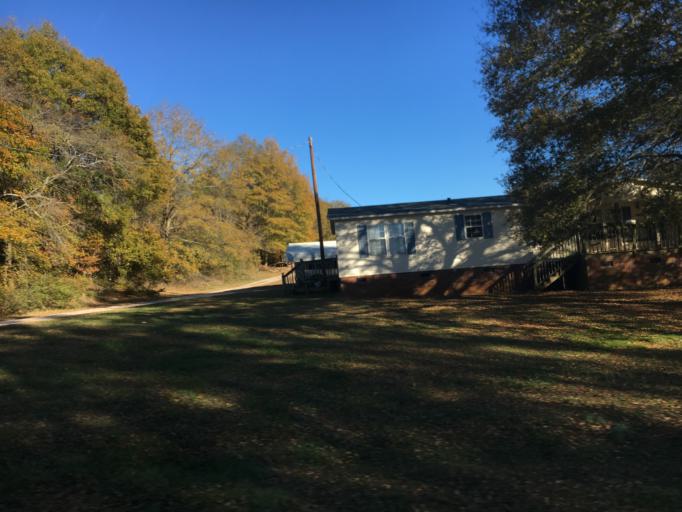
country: US
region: South Carolina
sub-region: Spartanburg County
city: Duncan
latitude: 34.9286
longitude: -82.1461
